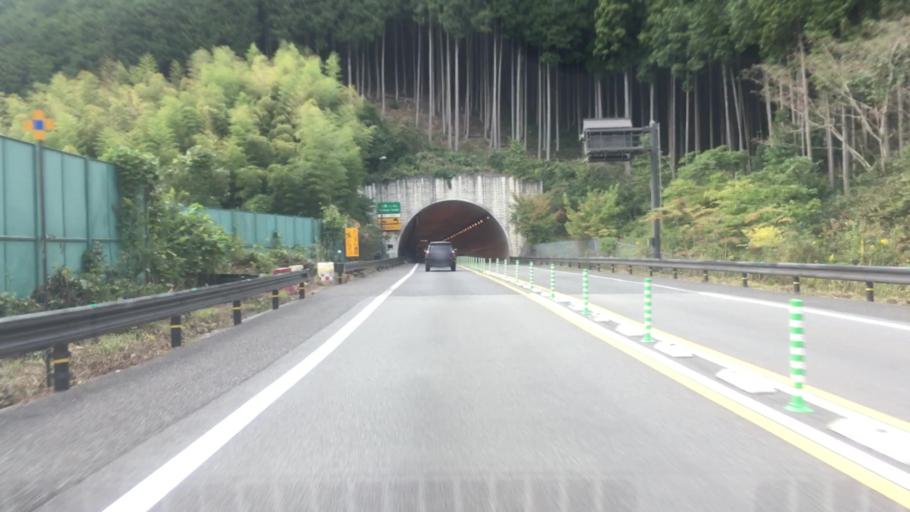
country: JP
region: Kyoto
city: Fukuchiyama
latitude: 35.2745
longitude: 134.9932
